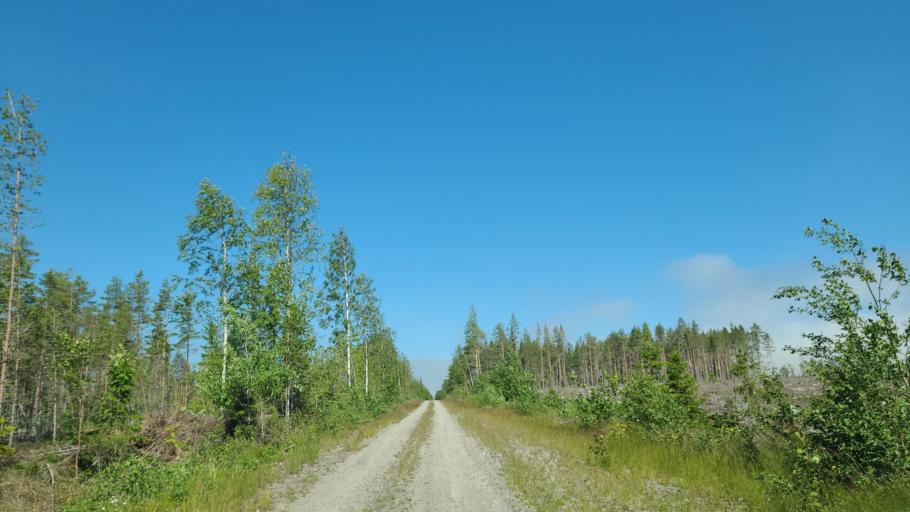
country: SE
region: Vaesternorrland
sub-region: OErnskoeldsviks Kommun
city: Husum
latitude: 63.4315
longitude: 19.2289
